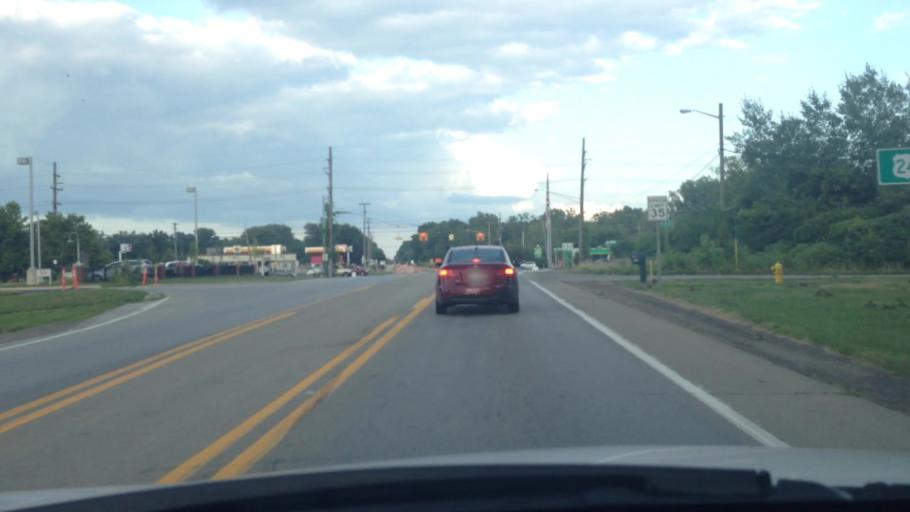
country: US
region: Michigan
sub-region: Wayne County
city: Woodhaven
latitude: 42.1672
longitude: -83.2686
